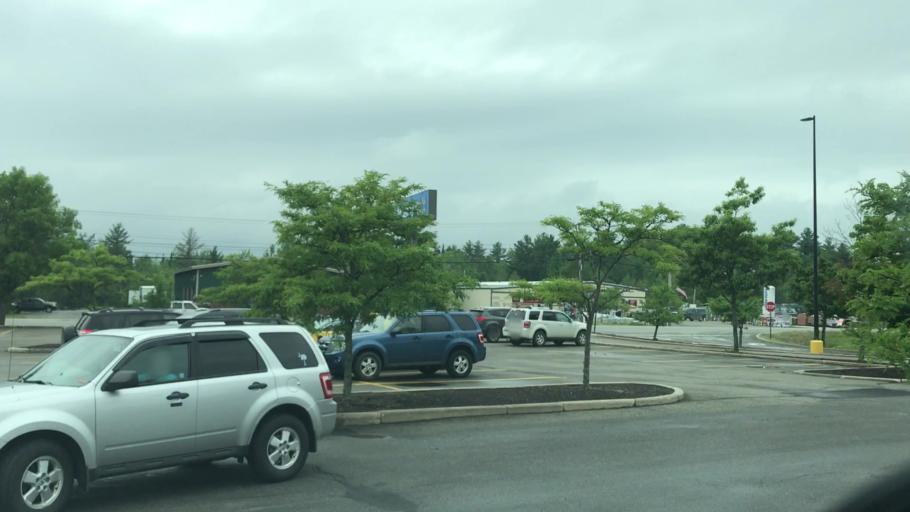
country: US
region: Maine
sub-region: Penobscot County
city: Lincoln
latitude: 45.3564
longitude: -68.5256
